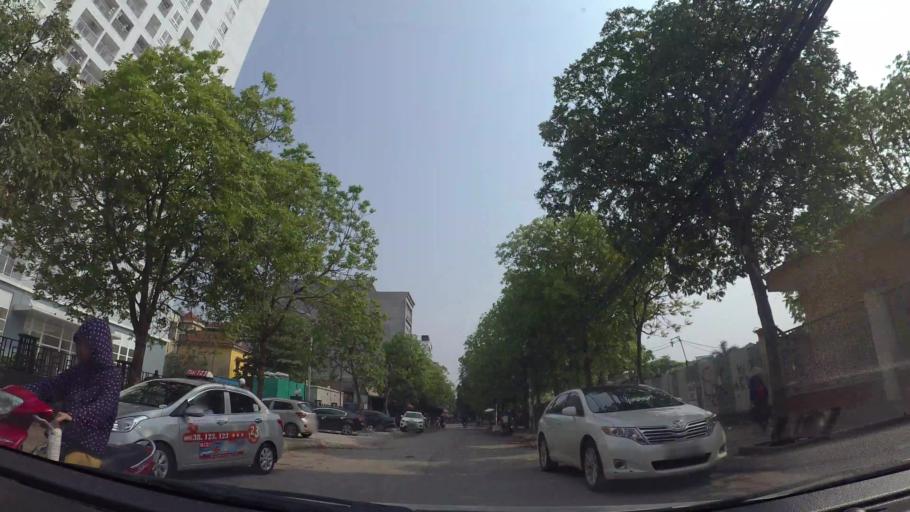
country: VN
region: Ha Noi
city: Tay Ho
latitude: 21.0646
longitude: 105.8077
